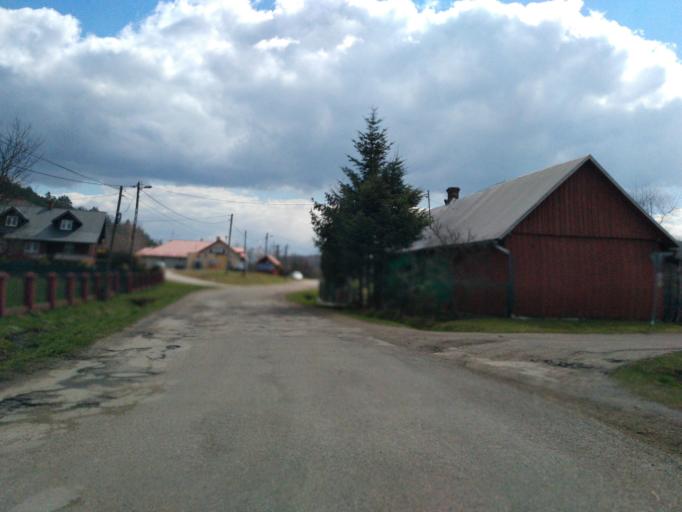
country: PL
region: Subcarpathian Voivodeship
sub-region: Powiat sanocki
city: Sanok
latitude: 49.6111
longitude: 22.2808
